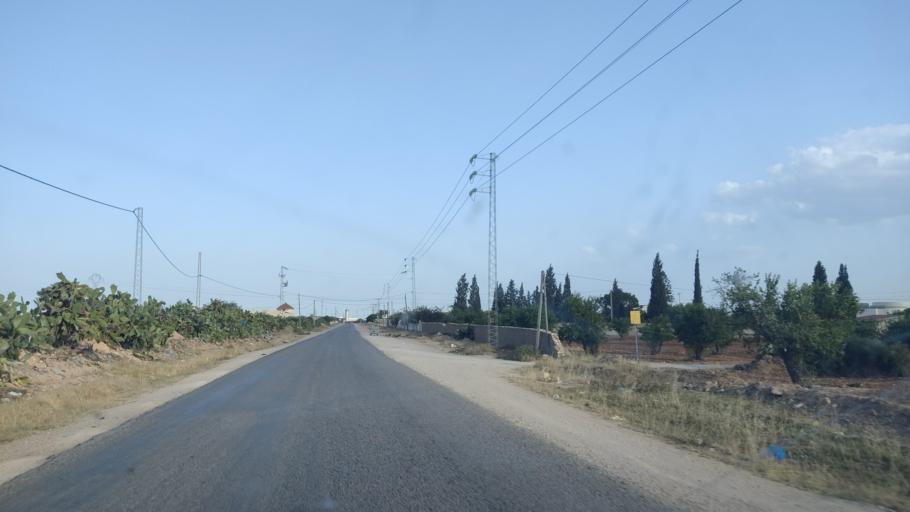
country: TN
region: Safaqis
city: Sfax
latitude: 34.8070
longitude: 10.6670
